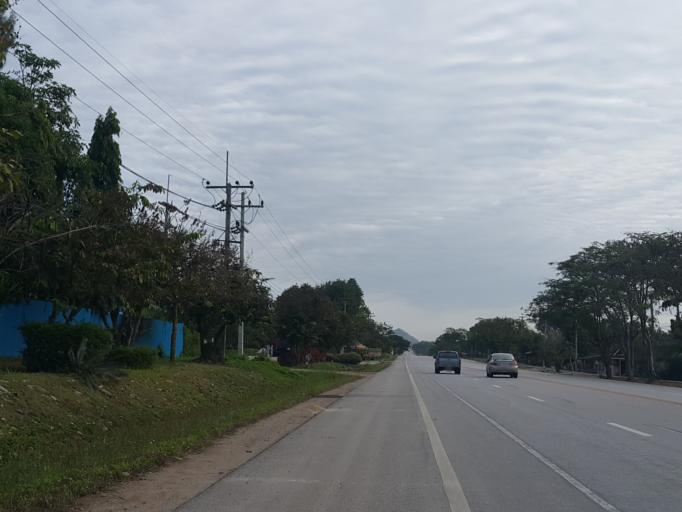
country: TH
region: Lampang
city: Mae Mo
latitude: 18.2434
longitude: 99.5921
